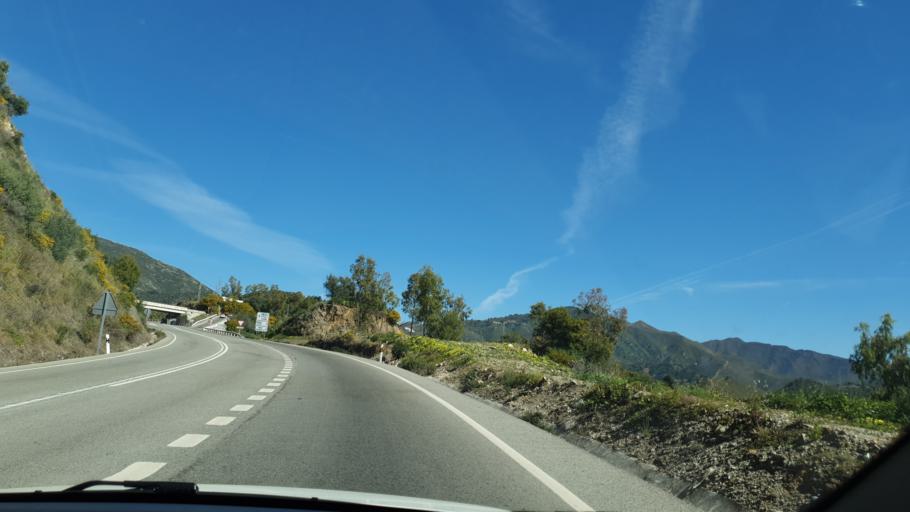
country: ES
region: Andalusia
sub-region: Provincia de Malaga
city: Ojen
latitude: 36.5454
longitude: -4.8616
